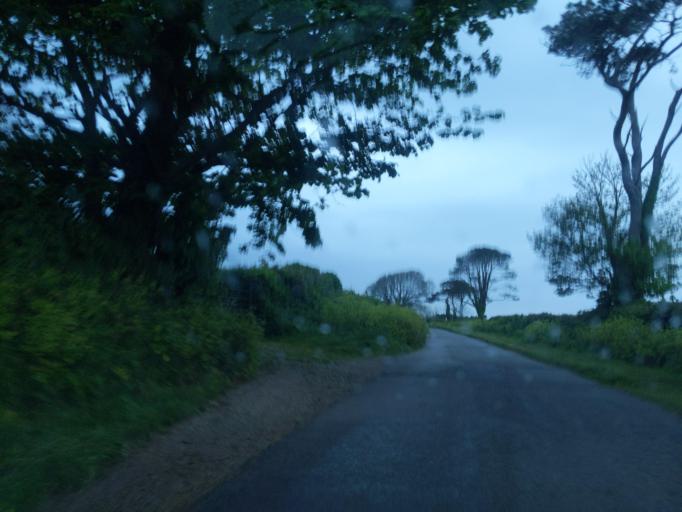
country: GB
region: England
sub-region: Devon
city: Dartmouth
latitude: 50.3596
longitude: -3.5473
